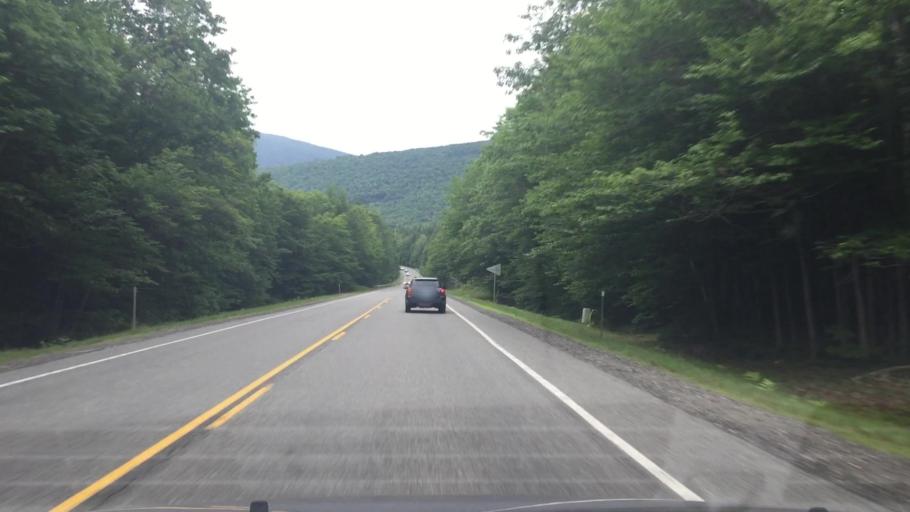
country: US
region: New Hampshire
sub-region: Carroll County
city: North Conway
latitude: 44.0939
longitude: -71.3545
